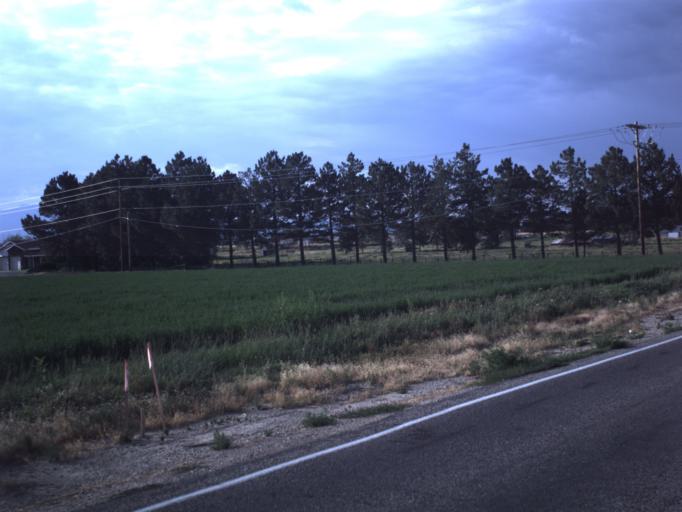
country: US
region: Utah
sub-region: Weber County
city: West Haven
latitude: 41.2207
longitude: -112.0929
